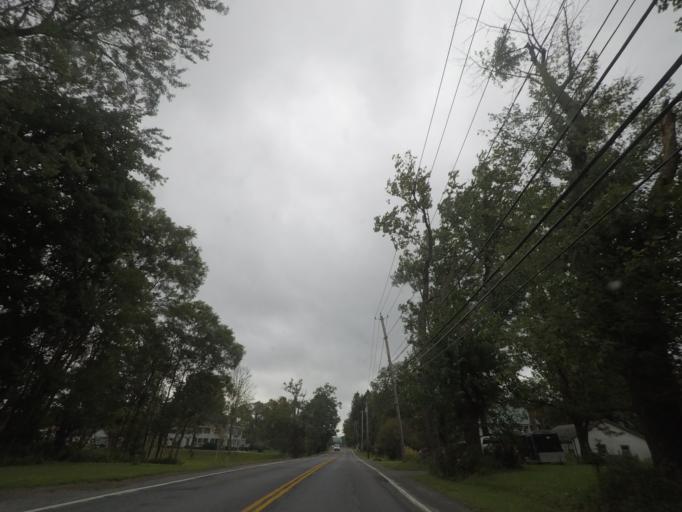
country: US
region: New York
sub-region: Rensselaer County
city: Hoosick Falls
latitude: 42.9218
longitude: -73.3487
